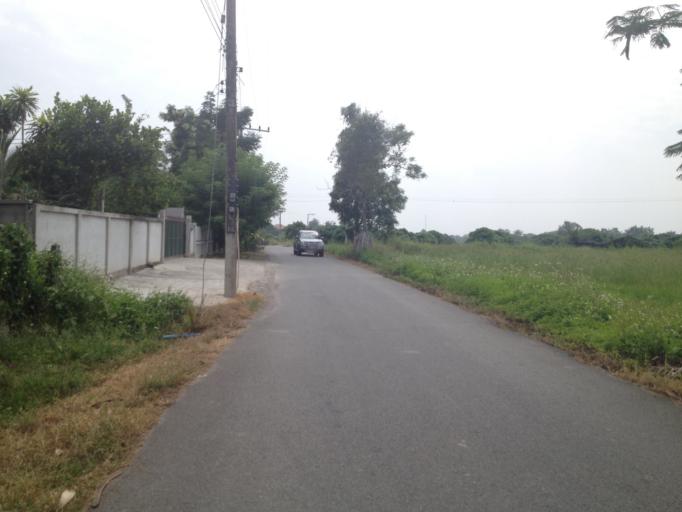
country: TH
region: Chiang Mai
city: Hang Dong
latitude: 18.6682
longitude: 98.8844
